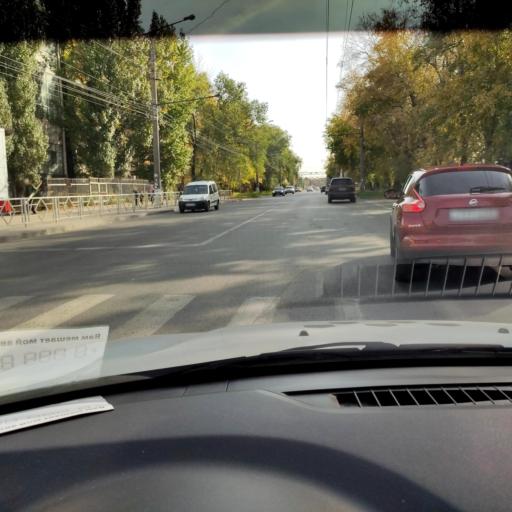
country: RU
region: Samara
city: Tol'yatti
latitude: 53.5122
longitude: 49.4299
